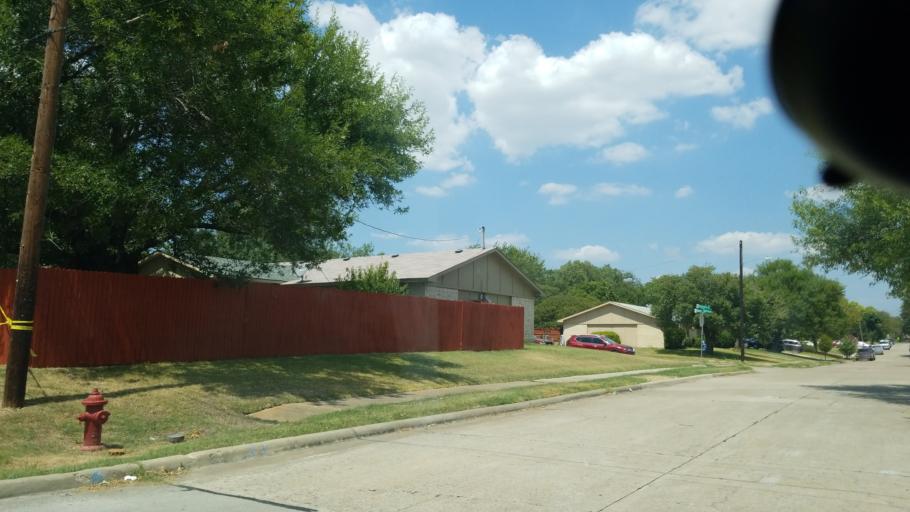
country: US
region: Texas
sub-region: Dallas County
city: Grand Prairie
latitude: 32.6989
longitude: -96.9902
